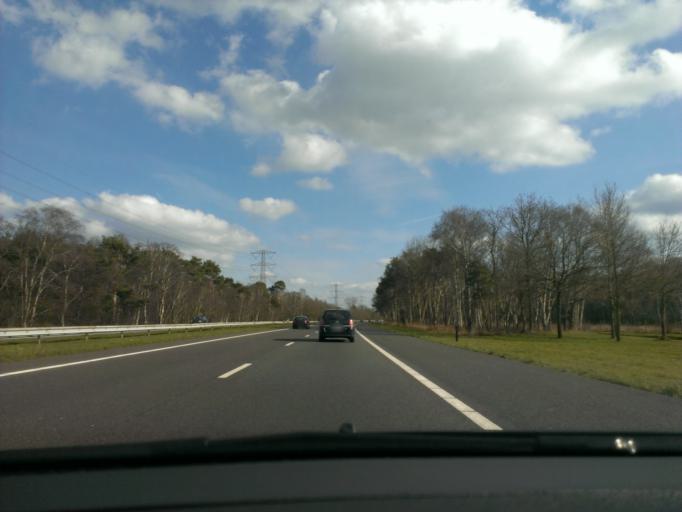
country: NL
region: Overijssel
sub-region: Gemeente Hengelo
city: Hengelo
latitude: 52.2266
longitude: 6.7881
